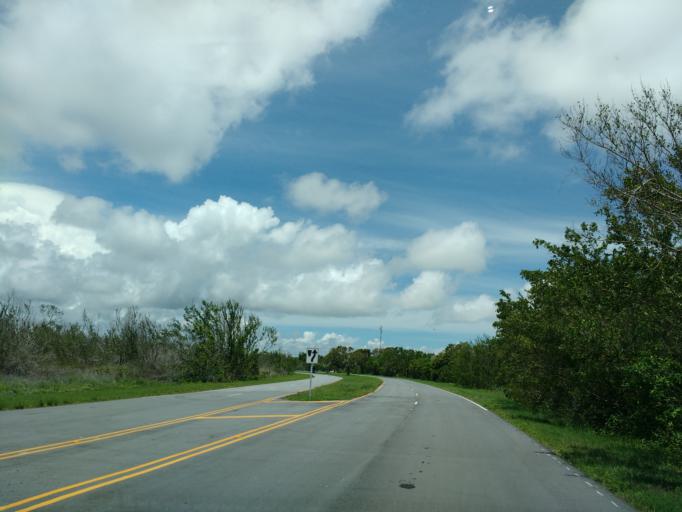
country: US
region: Florida
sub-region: Monroe County
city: Islamorada
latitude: 25.1396
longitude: -80.9293
